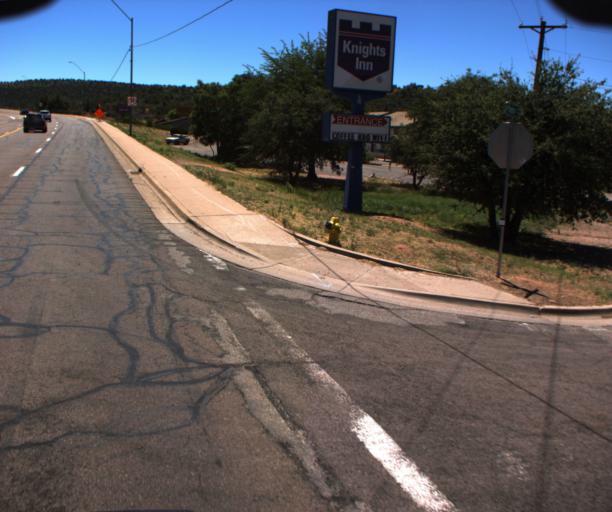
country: US
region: Arizona
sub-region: Gila County
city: Payson
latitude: 34.2265
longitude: -111.3302
